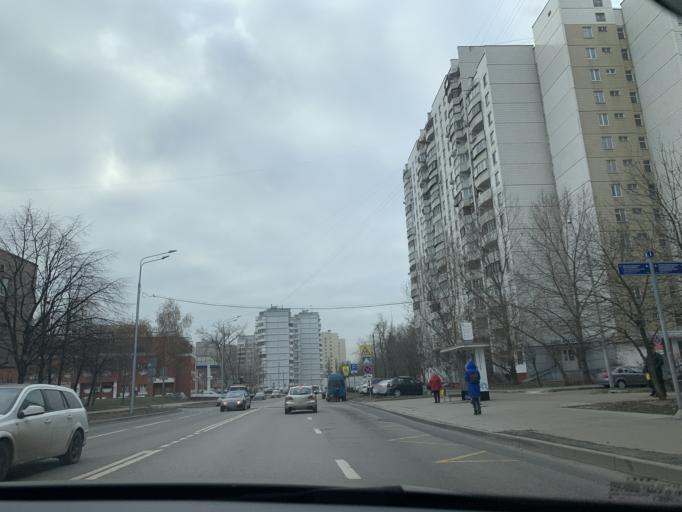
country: RU
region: Moscow
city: Likhobory
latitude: 55.8605
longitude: 37.5678
